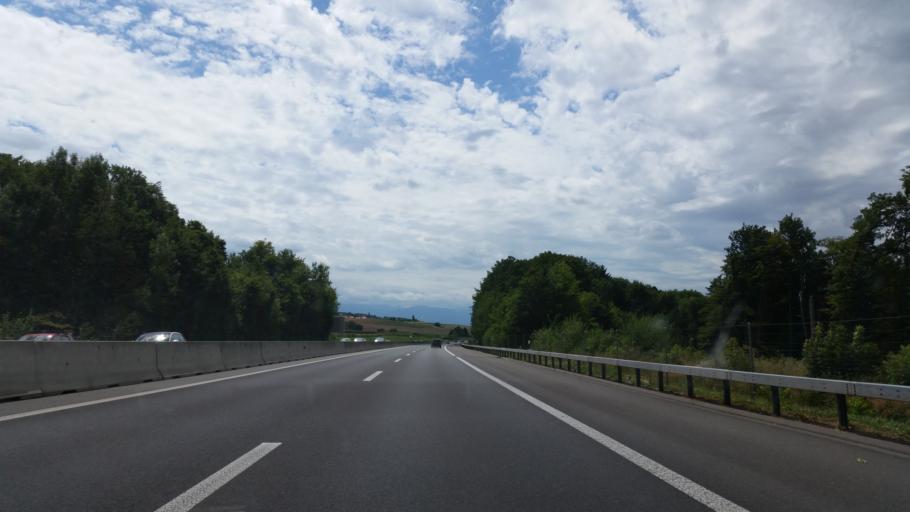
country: CH
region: Vaud
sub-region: Gros-de-Vaud District
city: Penthalaz
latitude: 46.6255
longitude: 6.5607
